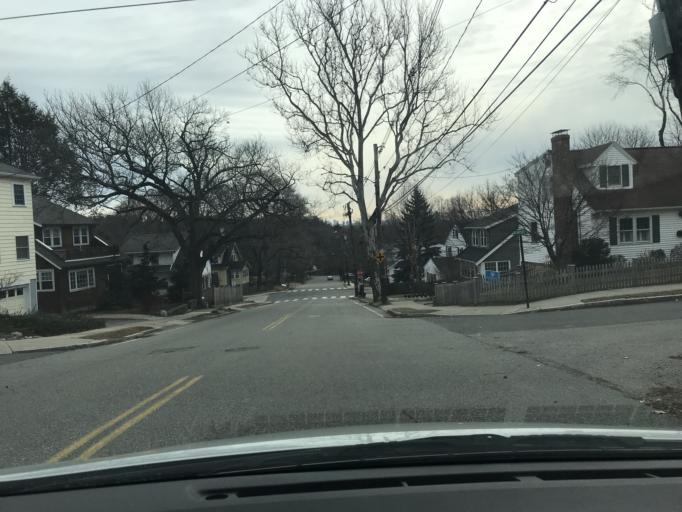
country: US
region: Massachusetts
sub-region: Middlesex County
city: Belmont
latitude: 42.4118
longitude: -71.1740
